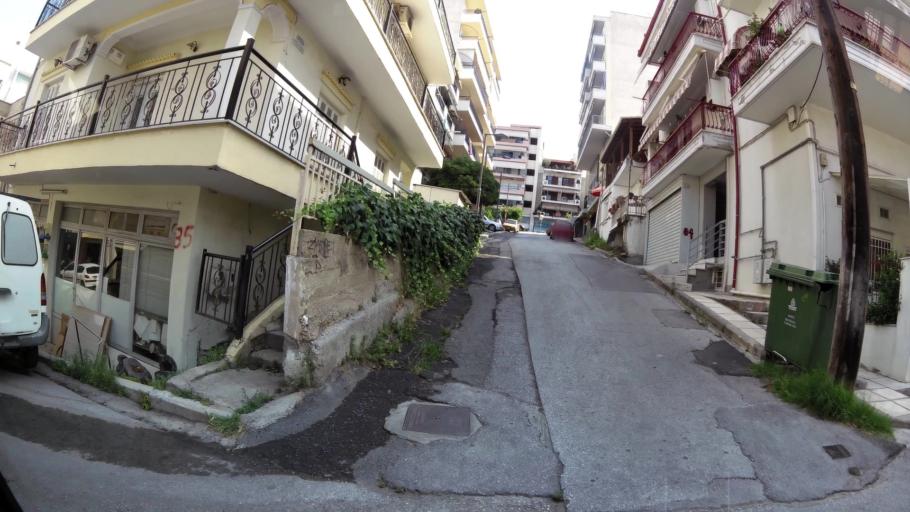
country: GR
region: Central Macedonia
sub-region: Nomos Thessalonikis
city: Sykies
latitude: 40.6527
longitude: 22.9538
